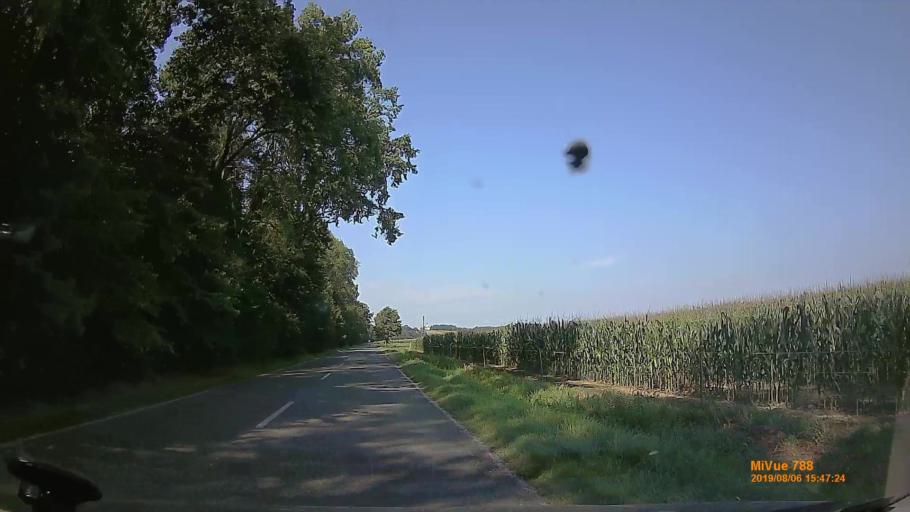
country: HU
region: Somogy
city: Csurgo
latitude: 46.2570
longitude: 17.0248
